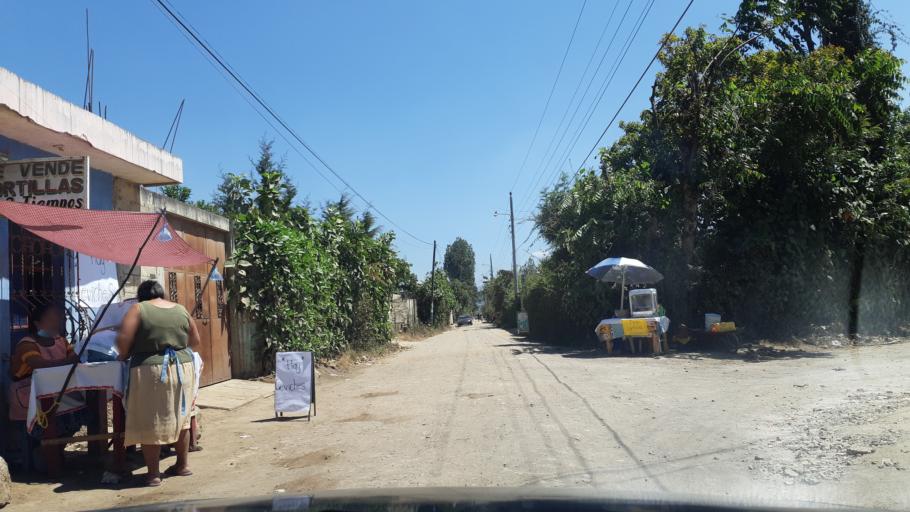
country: GT
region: Chimaltenango
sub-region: Municipio de Chimaltenango
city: Chimaltenango
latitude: 14.6503
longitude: -90.8109
